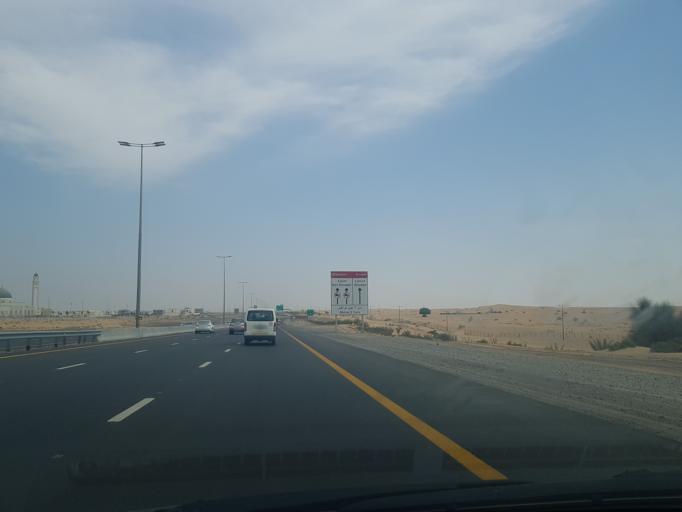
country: AE
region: Ash Shariqah
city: Sharjah
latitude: 25.2279
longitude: 55.5936
